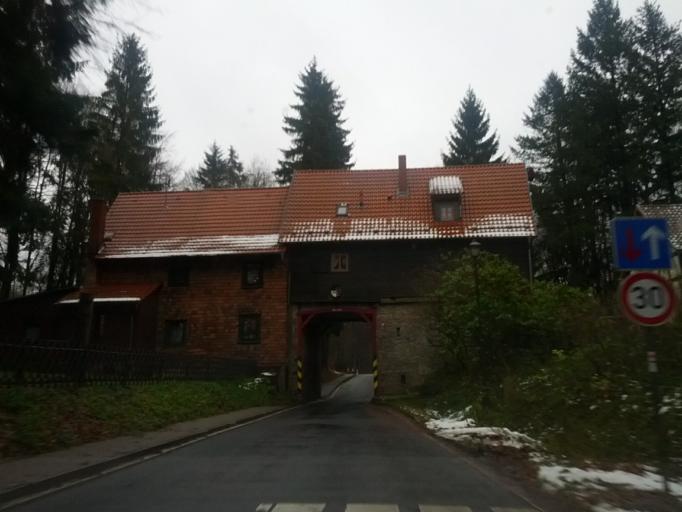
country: DE
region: Thuringia
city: Heyerode
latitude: 51.1679
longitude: 10.3336
